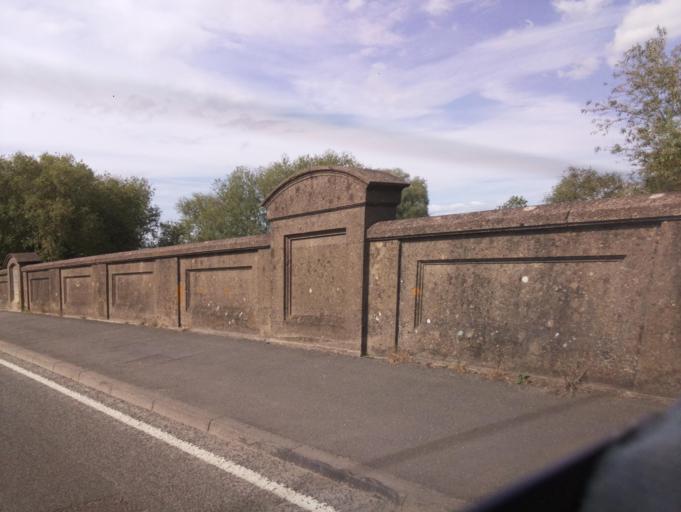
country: GB
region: England
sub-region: Worcestershire
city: Pershore
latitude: 52.1042
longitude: -2.0714
